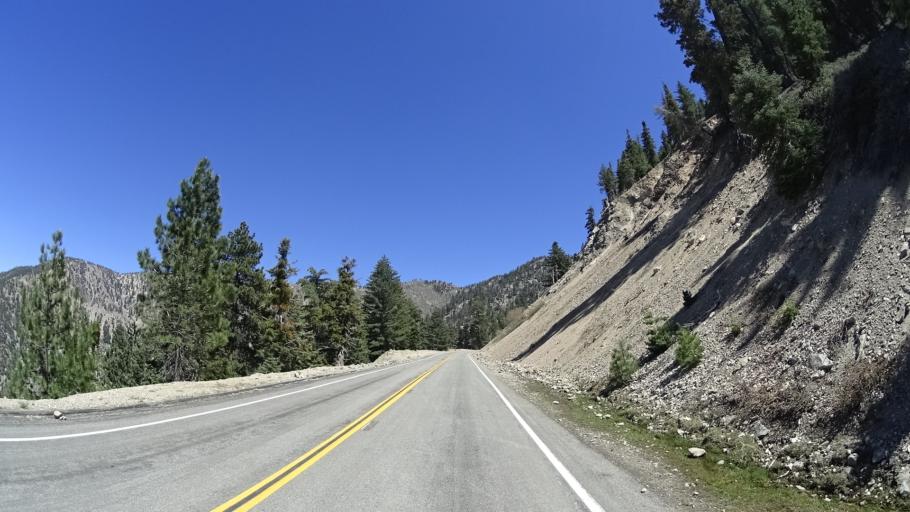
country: US
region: California
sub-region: San Bernardino County
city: Wrightwood
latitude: 34.3494
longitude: -117.8303
